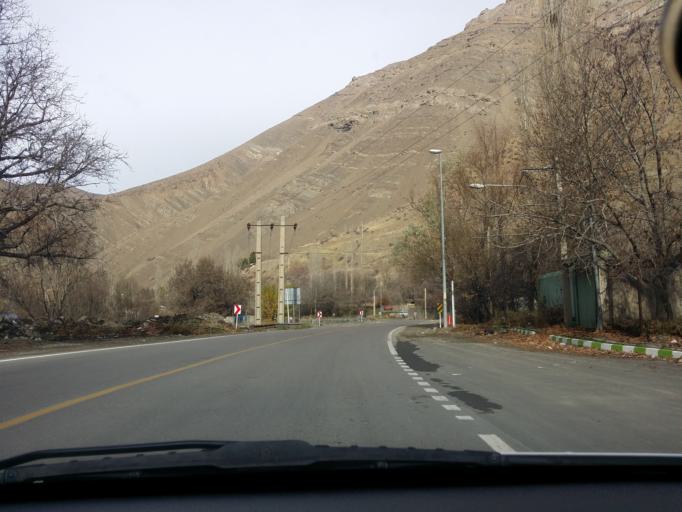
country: IR
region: Alborz
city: Karaj
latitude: 36.0378
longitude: 51.1910
